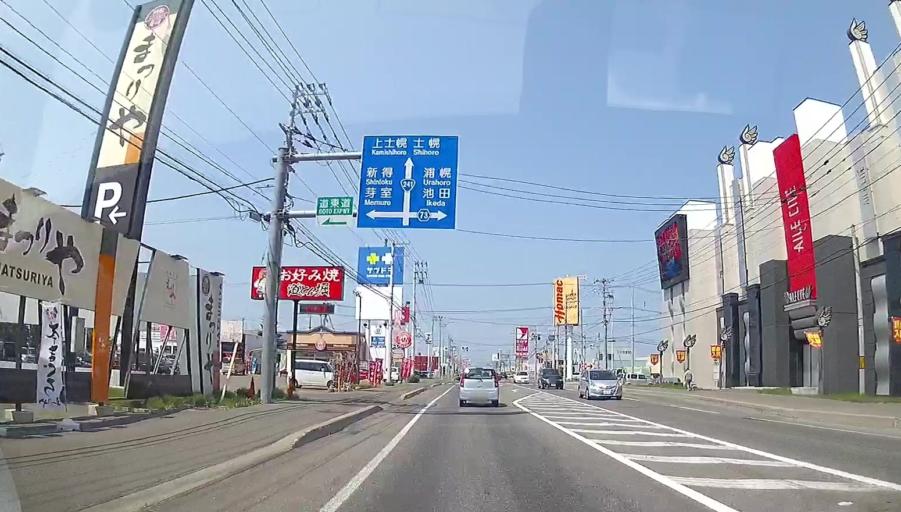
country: JP
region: Hokkaido
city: Otofuke
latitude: 42.9565
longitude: 143.2058
